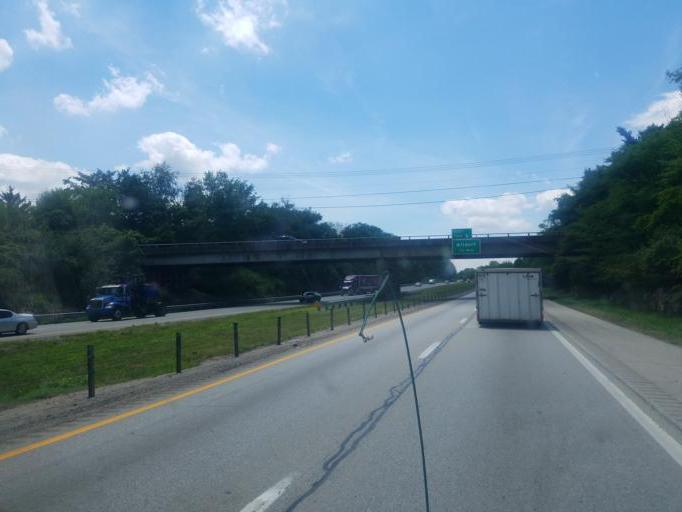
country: US
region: Kentucky
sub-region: Jefferson County
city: Northfield
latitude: 38.2941
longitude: -85.6324
